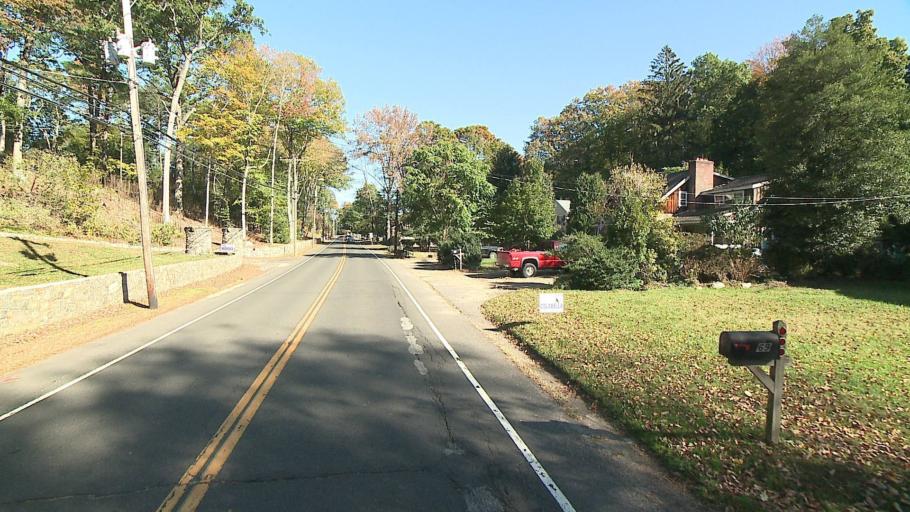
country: US
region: Connecticut
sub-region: Fairfield County
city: Westport
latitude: 41.1375
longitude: -73.3541
